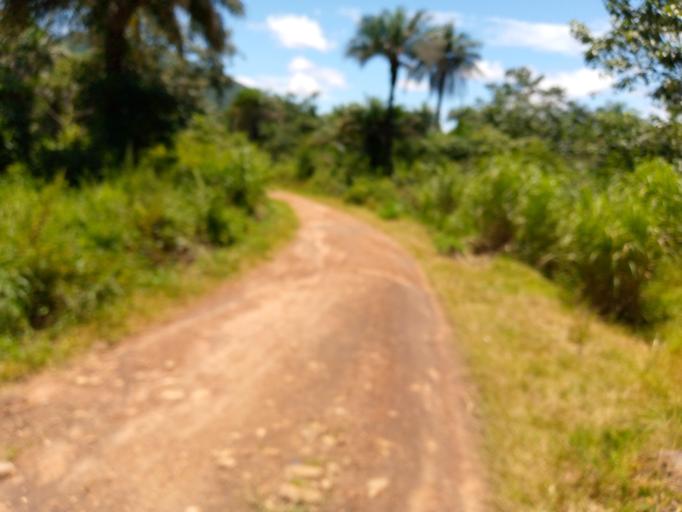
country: SL
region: Northern Province
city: Binkolo
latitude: 9.0981
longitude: -12.1433
